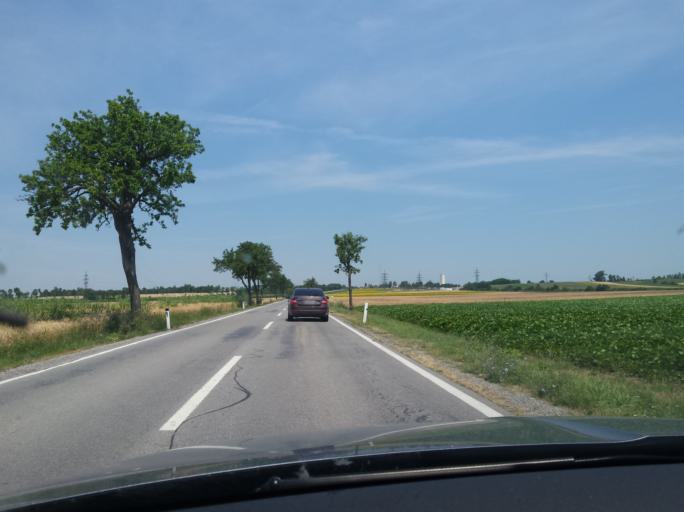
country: AT
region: Lower Austria
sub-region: Politischer Bezirk Bruck an der Leitha
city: Rohrau
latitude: 48.0851
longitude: 16.8629
